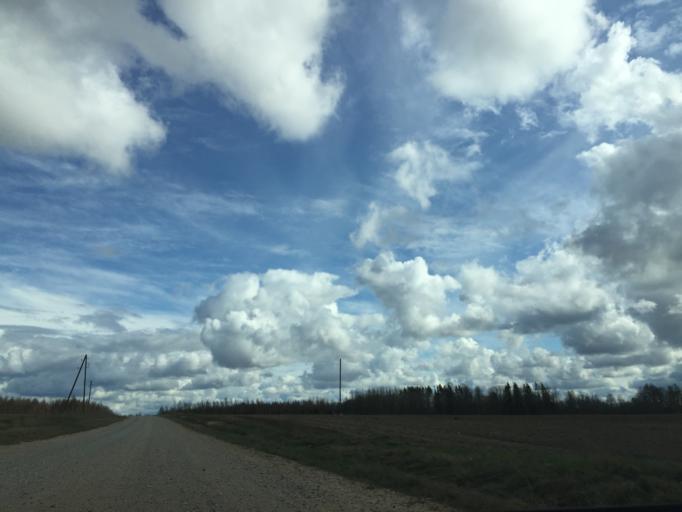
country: LV
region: Limbazu Rajons
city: Limbazi
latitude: 57.6062
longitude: 24.7958
